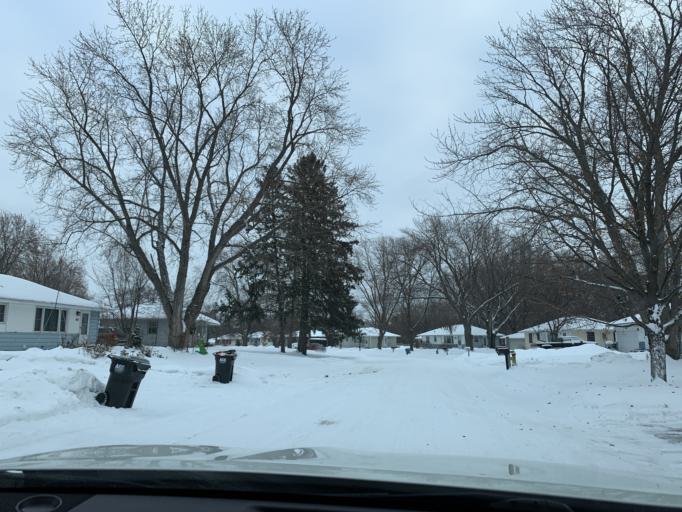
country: US
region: Minnesota
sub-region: Anoka County
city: Coon Rapids
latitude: 45.1688
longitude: -93.2910
